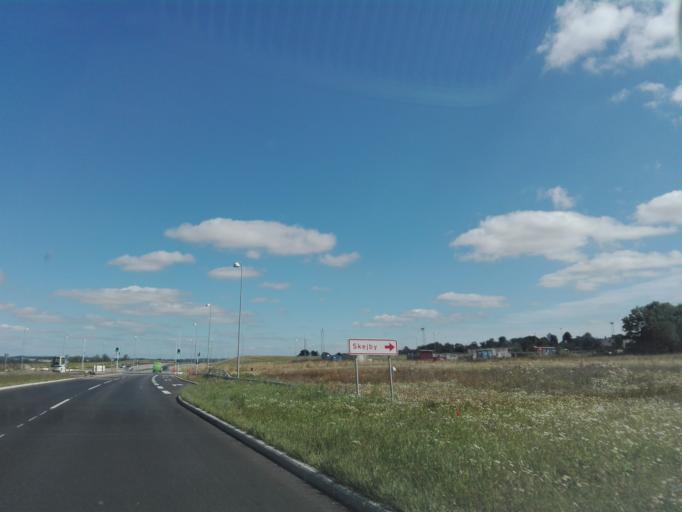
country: DK
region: Central Jutland
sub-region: Arhus Kommune
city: Trige
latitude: 56.1984
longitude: 10.1645
